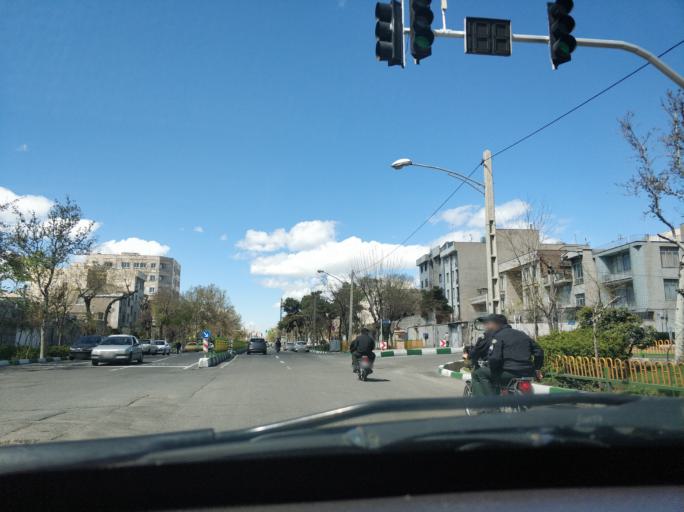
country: IR
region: Tehran
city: Tehran
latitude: 35.7207
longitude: 51.4877
